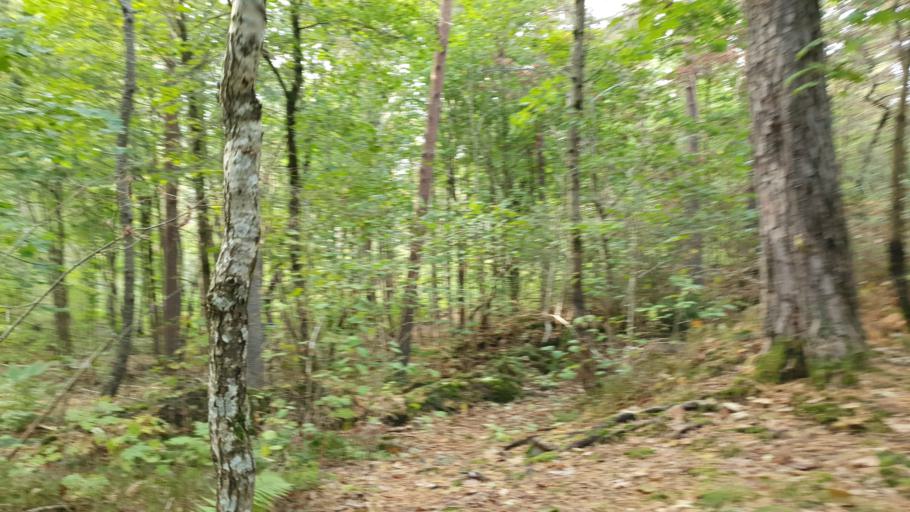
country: NO
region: Vestfold
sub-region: Tonsberg
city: Tonsberg
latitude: 59.2825
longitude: 10.4242
